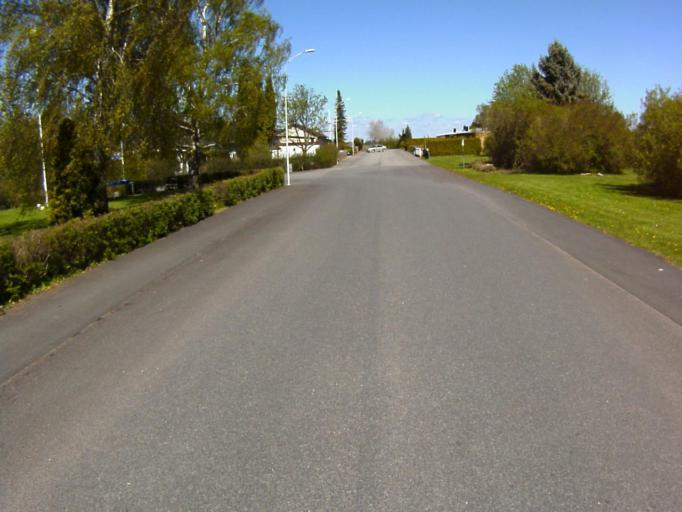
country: SE
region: Skane
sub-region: Kristianstads Kommun
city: Kristianstad
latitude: 56.0495
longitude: 14.2105
